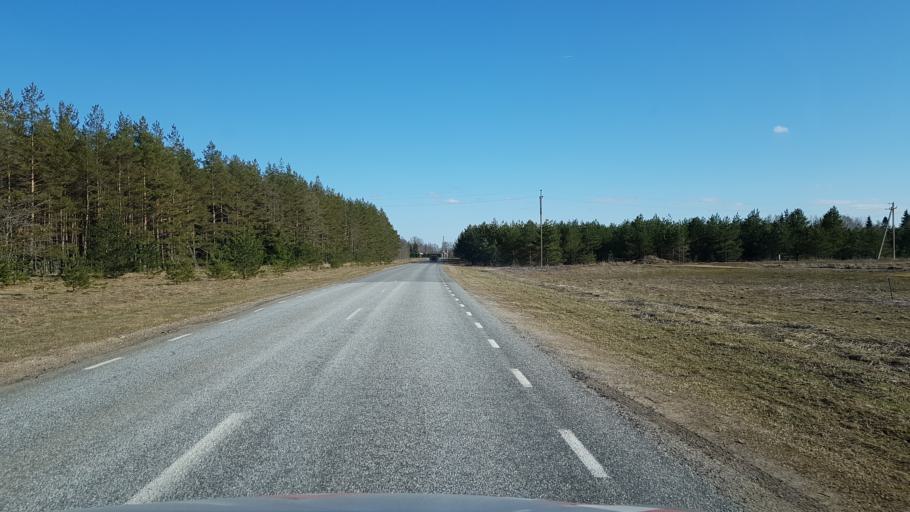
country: EE
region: Laeaene-Virumaa
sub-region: Haljala vald
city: Haljala
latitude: 59.4679
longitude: 26.1796
